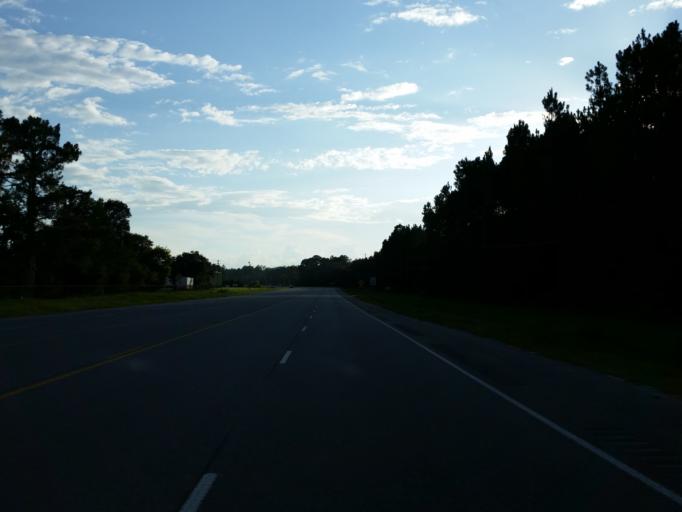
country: US
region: Georgia
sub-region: Clinch County
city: Homerville
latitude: 31.0309
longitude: -82.7747
